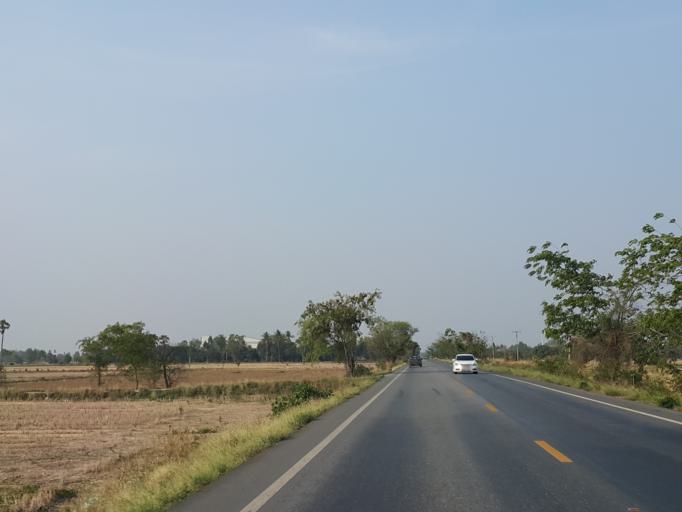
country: TH
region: Chai Nat
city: Sankhaburi
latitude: 14.9828
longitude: 100.1076
